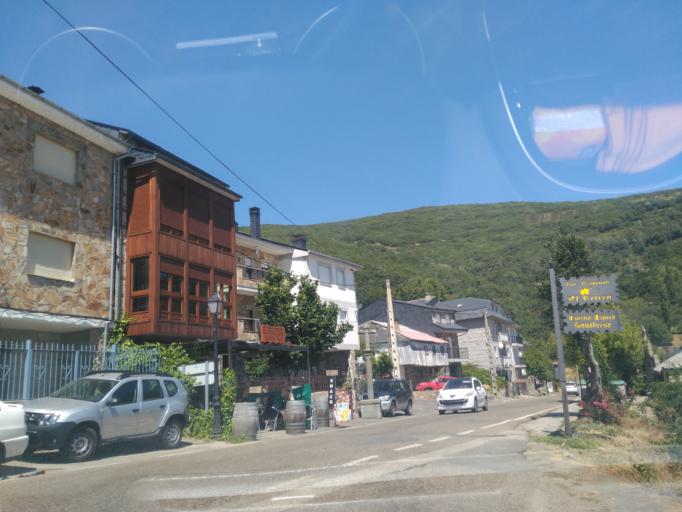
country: ES
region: Castille and Leon
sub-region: Provincia de Zamora
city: Cobreros
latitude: 42.1360
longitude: -6.7206
